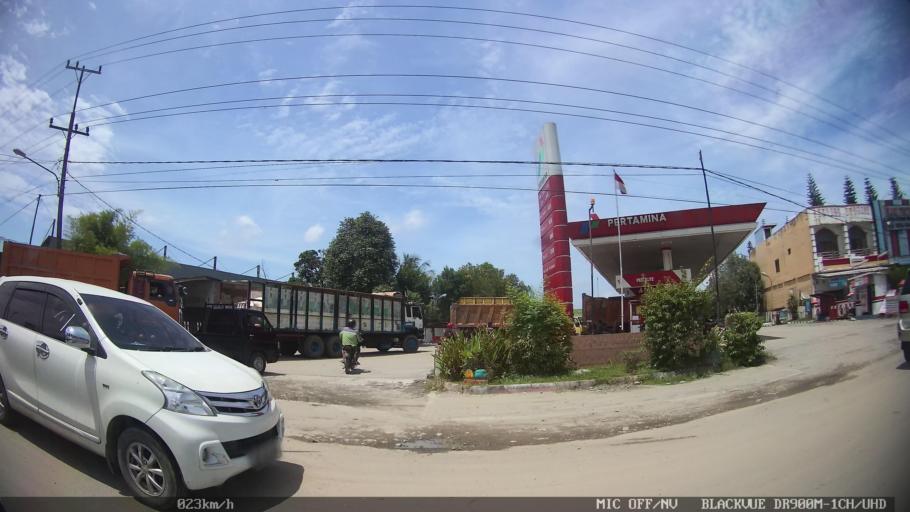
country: ID
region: North Sumatra
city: Perbaungan
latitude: 3.5451
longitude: 98.8803
